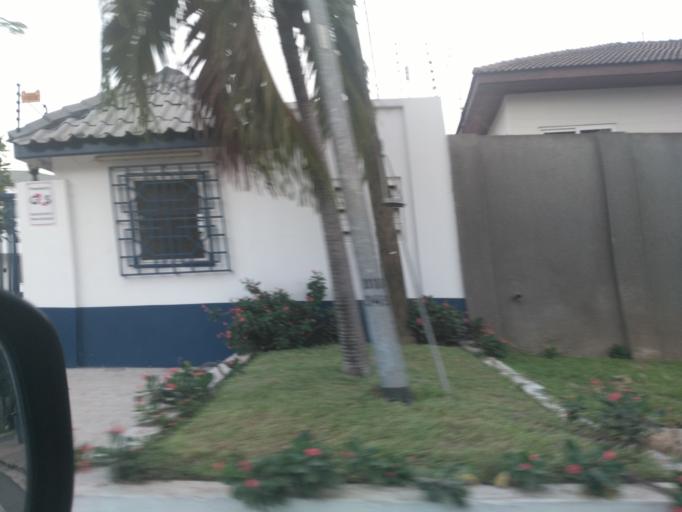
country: GH
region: Greater Accra
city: Accra
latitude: 5.6052
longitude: -0.1822
